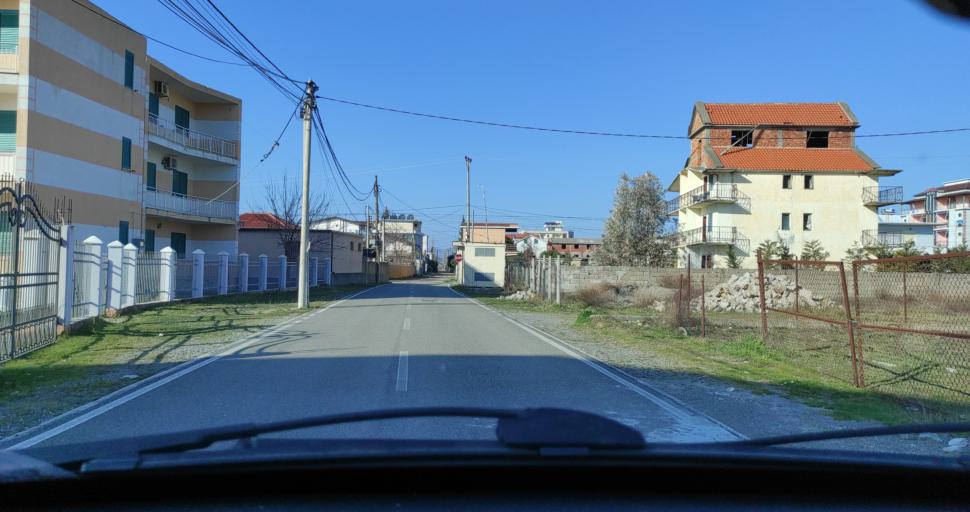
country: AL
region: Shkoder
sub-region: Rrethi i Shkodres
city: Velipoje
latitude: 41.8653
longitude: 19.4302
